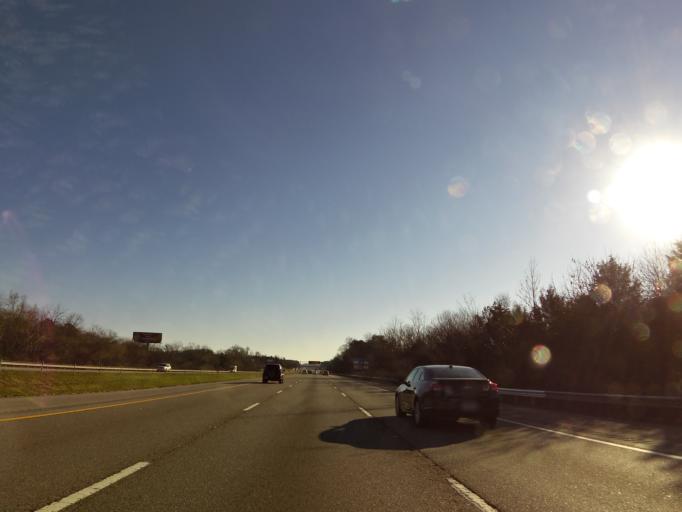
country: US
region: Tennessee
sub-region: Knox County
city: Mascot
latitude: 36.0054
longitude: -83.8024
